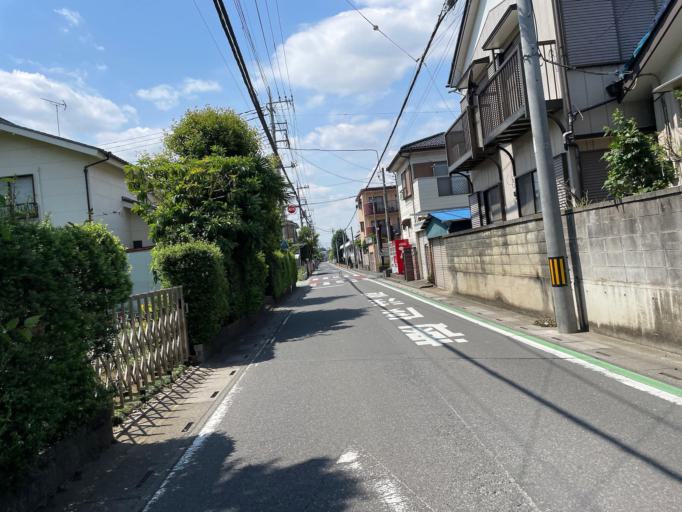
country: JP
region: Saitama
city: Iwatsuki
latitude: 35.9492
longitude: 139.7055
